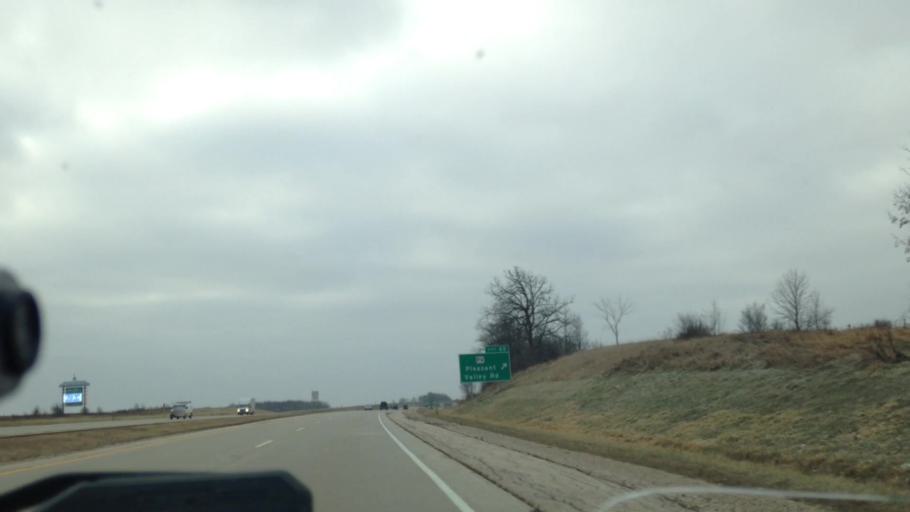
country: US
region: Wisconsin
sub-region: Washington County
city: Jackson
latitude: 43.3602
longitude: -88.1921
